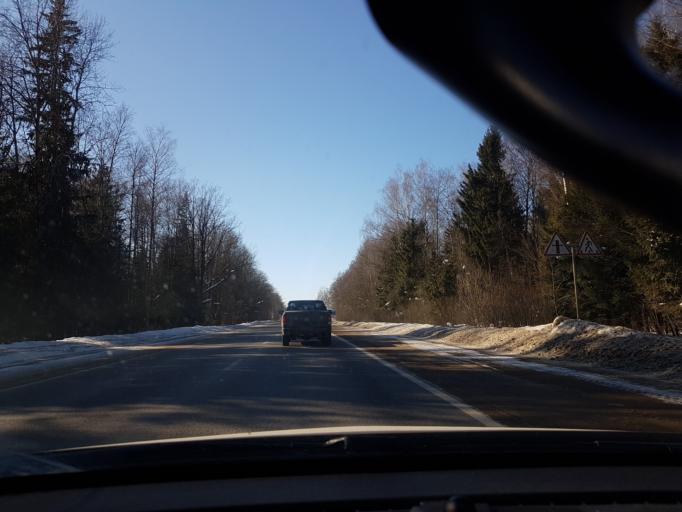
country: RU
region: Moskovskaya
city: Kostrovo
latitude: 55.9149
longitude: 36.6970
